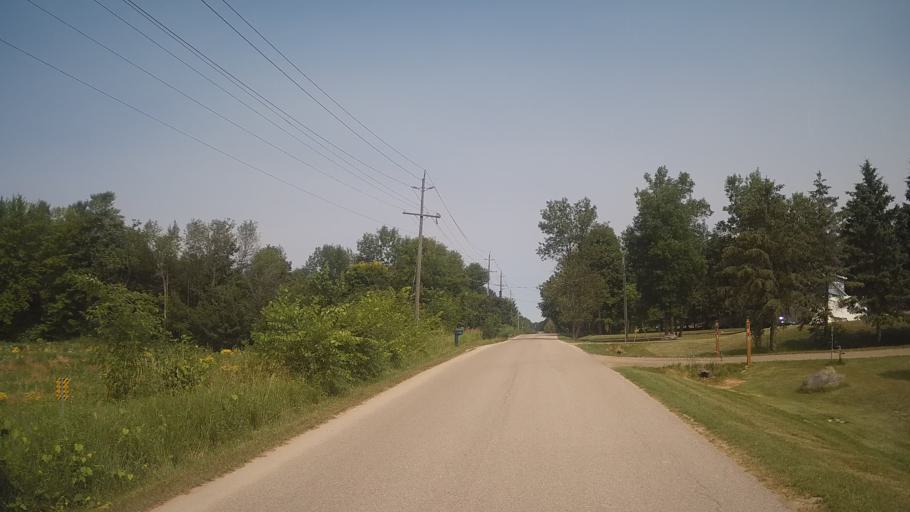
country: CA
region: Ontario
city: Barrie
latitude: 44.4459
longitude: -79.6222
